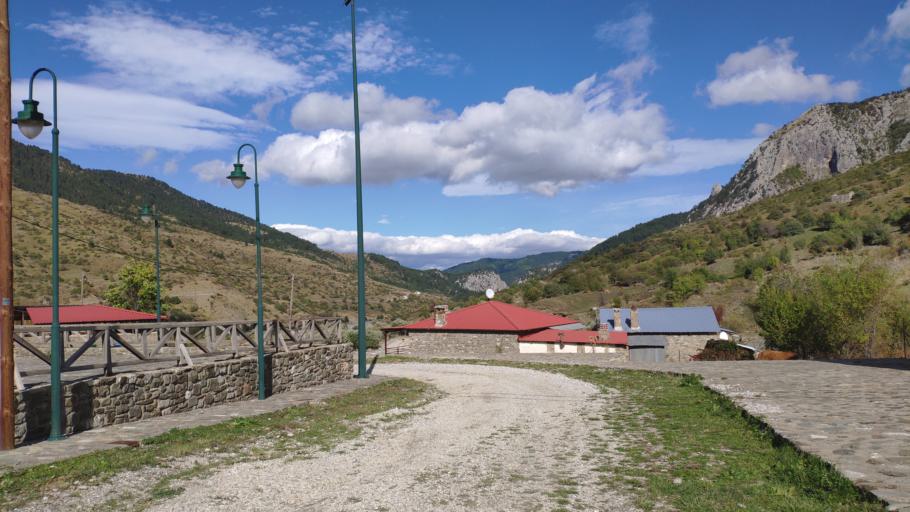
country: AL
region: Korce
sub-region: Rrethi i Devollit
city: Miras
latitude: 40.3913
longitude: 20.8359
